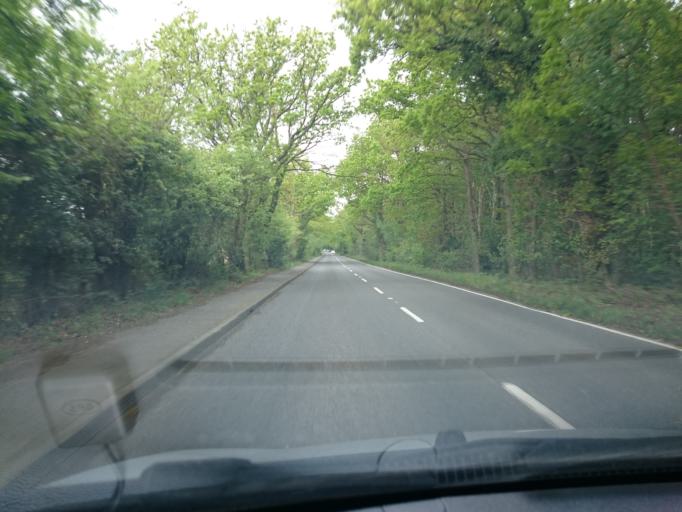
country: GB
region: England
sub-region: Surrey
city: Normandy
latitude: 51.2549
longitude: -0.6846
